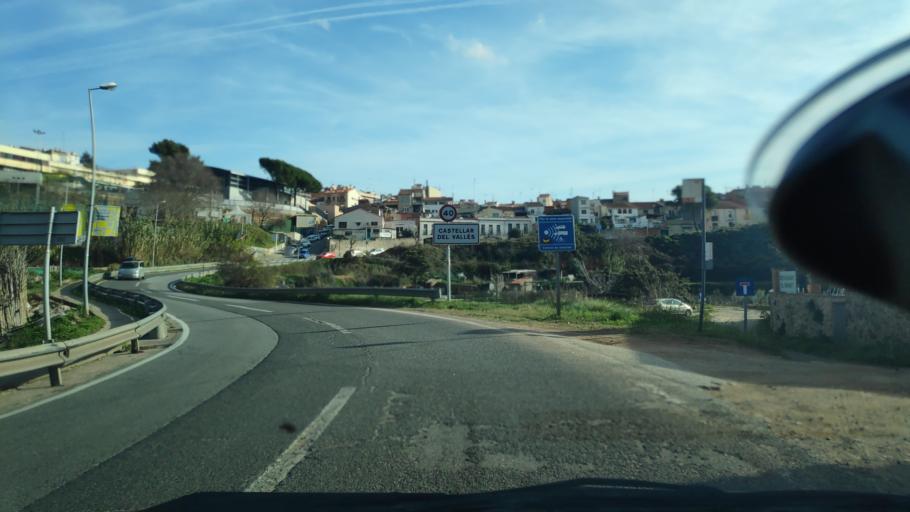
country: ES
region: Catalonia
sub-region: Provincia de Barcelona
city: Castellar del Valles
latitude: 41.6165
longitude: 2.0820
